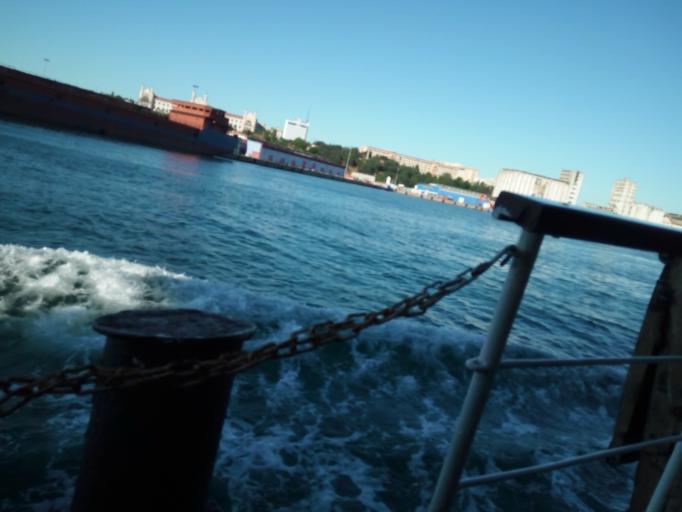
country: TR
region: Istanbul
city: UEskuedar
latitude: 40.9999
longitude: 29.0110
